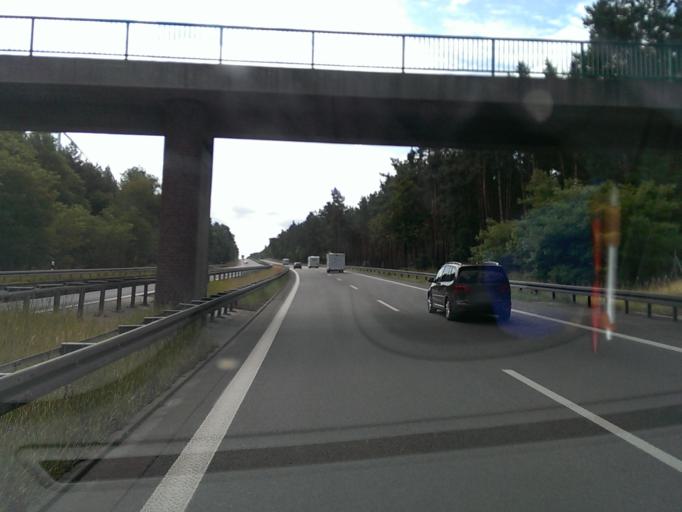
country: DE
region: Brandenburg
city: Bronkow
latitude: 51.7375
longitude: 13.8648
